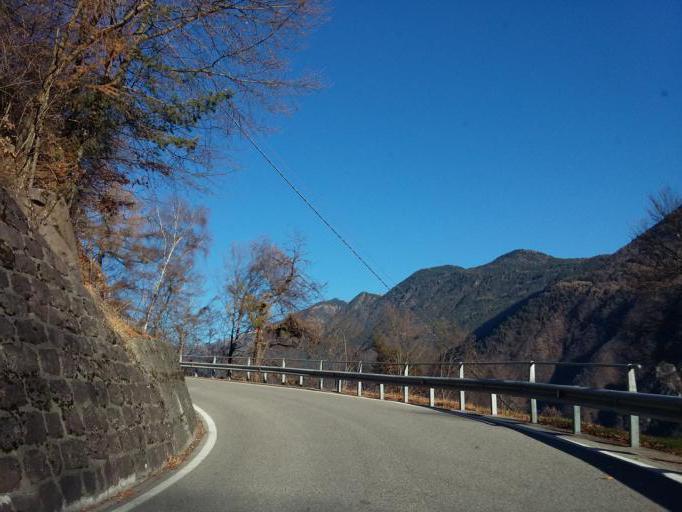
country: IT
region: Trentino-Alto Adige
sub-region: Provincia di Trento
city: Brione
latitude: 45.8943
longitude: 10.5976
